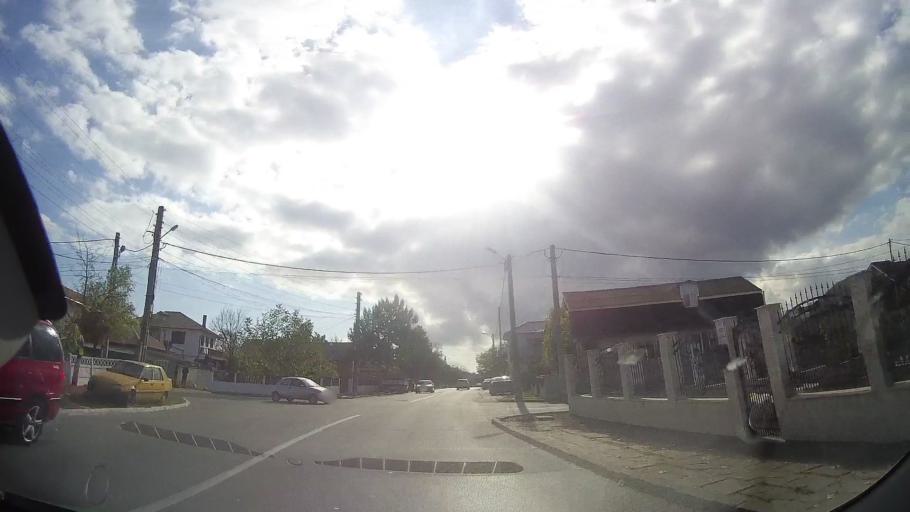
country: RO
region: Constanta
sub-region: Oras Techirghiol
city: Techirghiol
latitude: 44.0611
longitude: 28.5992
